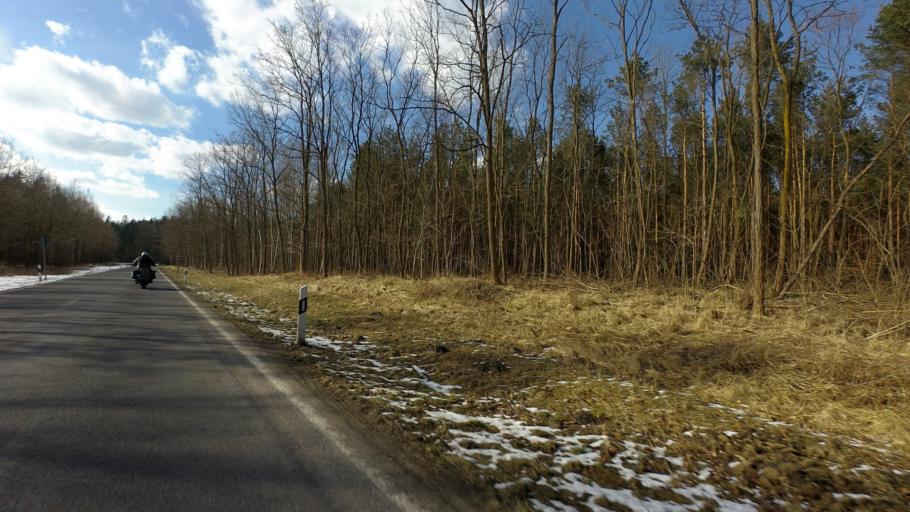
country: DE
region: Brandenburg
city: Wandlitz
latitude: 52.7707
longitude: 13.5057
